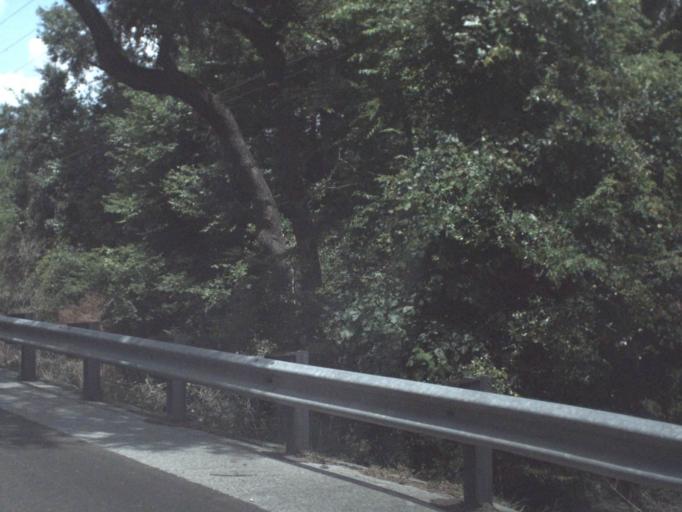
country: US
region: Florida
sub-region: Levy County
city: Williston
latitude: 29.4192
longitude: -82.4553
